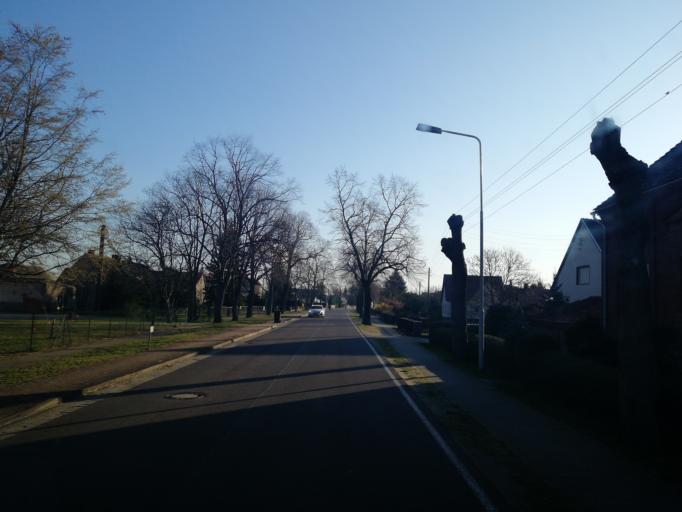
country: DE
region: Brandenburg
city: Drahnsdorf
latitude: 51.9197
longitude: 13.5966
